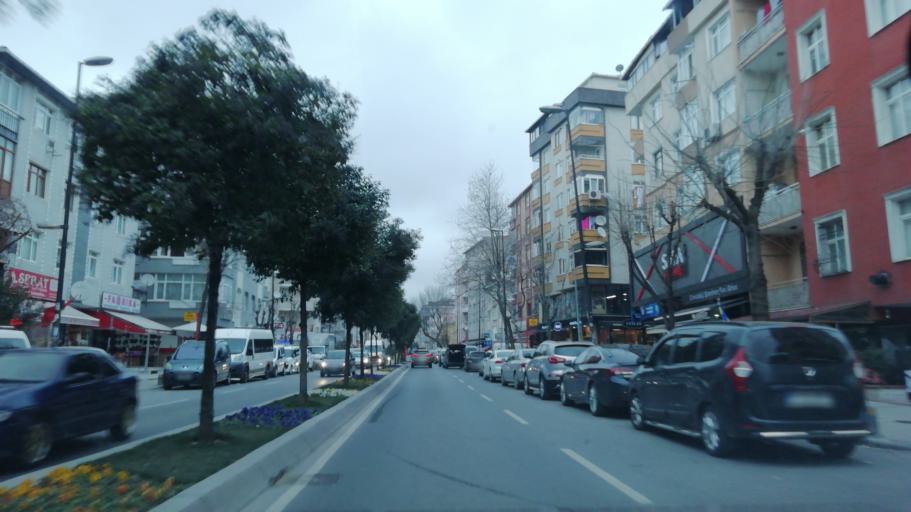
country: TR
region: Istanbul
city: Bahcelievler
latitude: 41.0078
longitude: 28.8497
